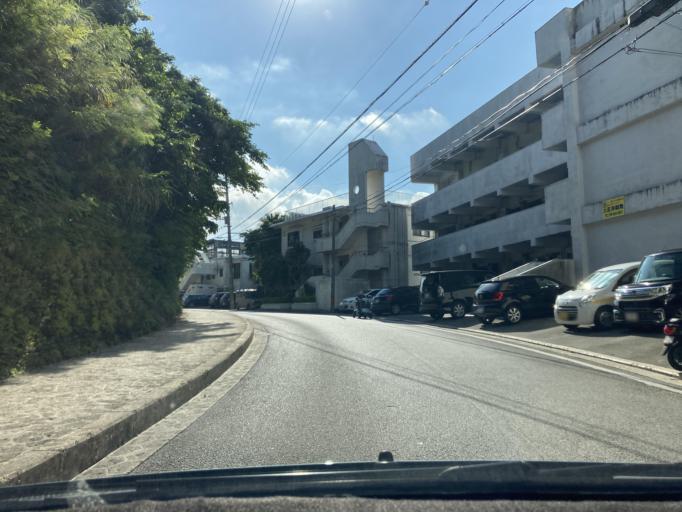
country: JP
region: Okinawa
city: Naha-shi
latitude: 26.2163
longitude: 127.7177
